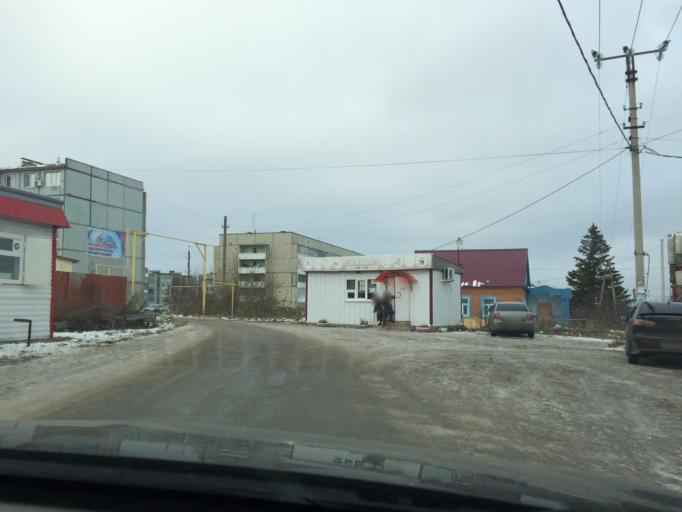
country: RU
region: Tula
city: Plavsk
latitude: 53.7028
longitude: 37.2785
